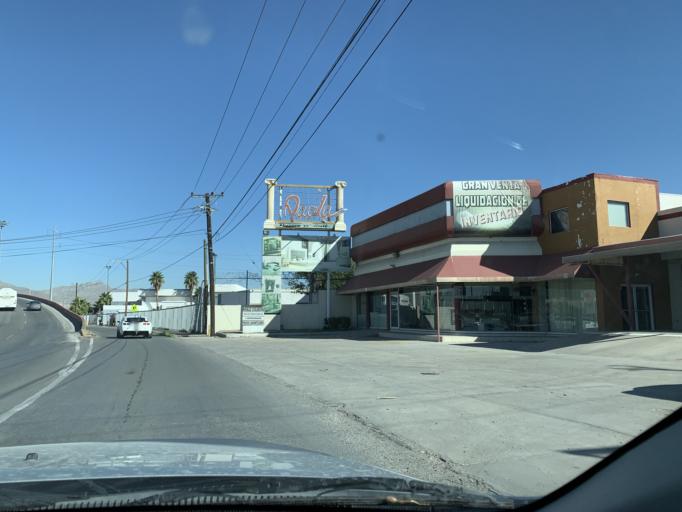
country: MX
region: Chihuahua
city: Ciudad Juarez
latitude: 31.7510
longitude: -106.4266
